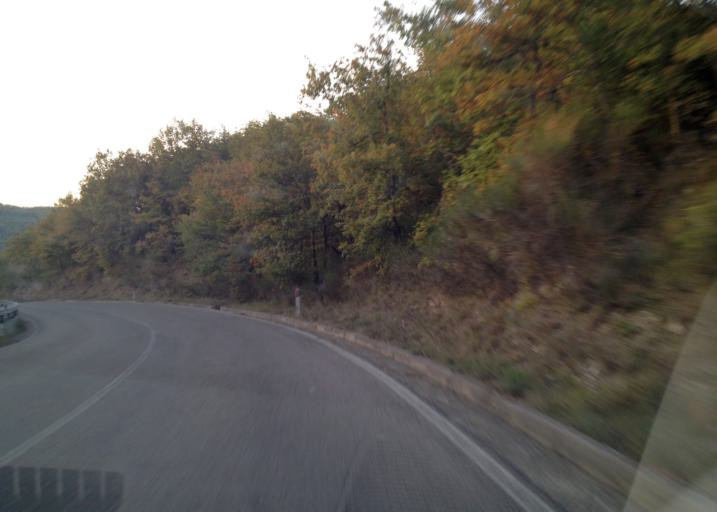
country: IT
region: Tuscany
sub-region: Provincia di Siena
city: Castellina in Chianti
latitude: 43.5038
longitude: 11.2947
